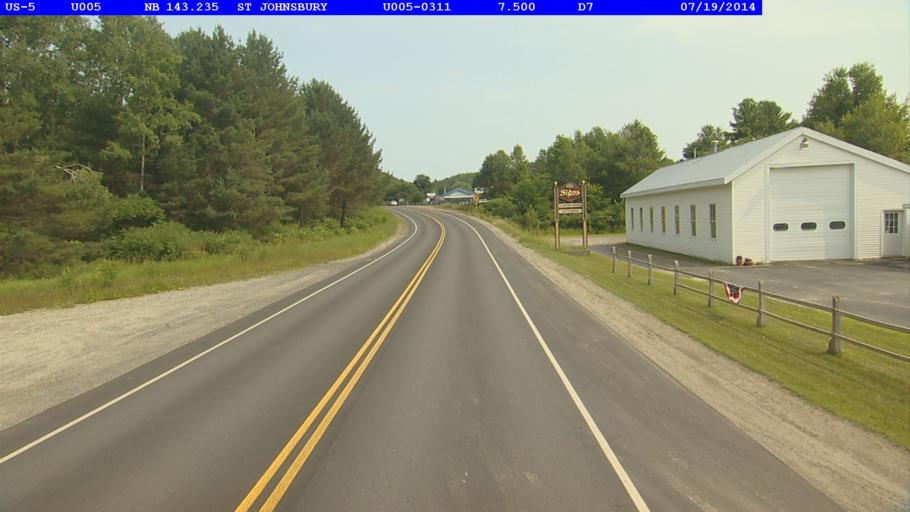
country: US
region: Vermont
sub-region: Caledonia County
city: Lyndon
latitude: 44.4961
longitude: -72.0045
